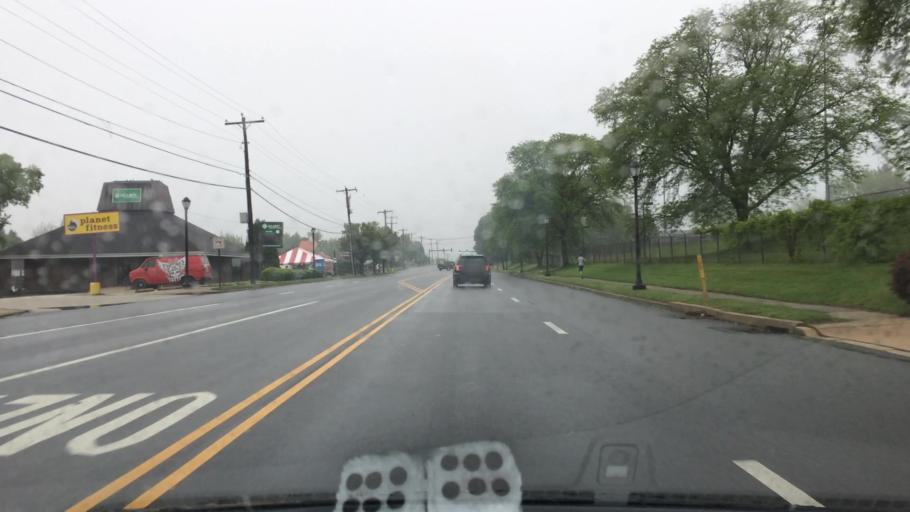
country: US
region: Pennsylvania
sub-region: Delaware County
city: Village Green-Green Ridge
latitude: 39.8638
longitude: -75.4278
